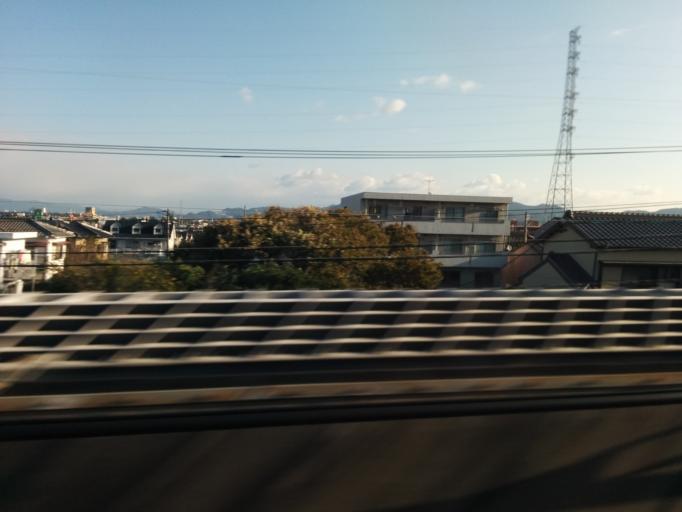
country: JP
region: Aichi
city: Toyohashi
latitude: 34.7444
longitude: 137.3958
